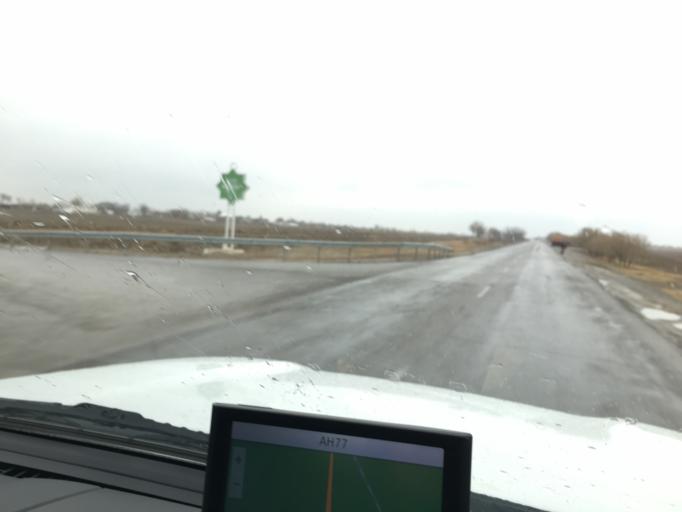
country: TM
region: Mary
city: Yoloeten
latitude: 37.3782
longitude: 62.2002
